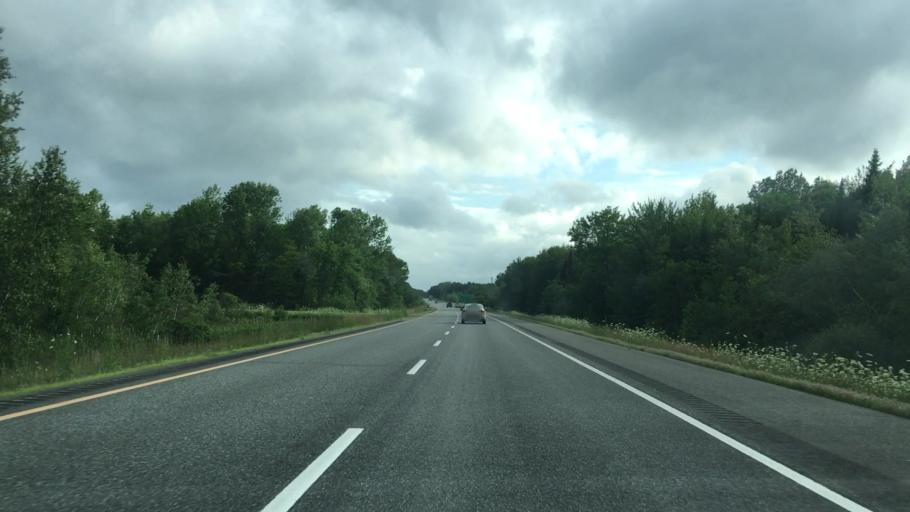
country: US
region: Maine
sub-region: Kennebec County
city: Clinton
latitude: 44.6461
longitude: -69.5219
